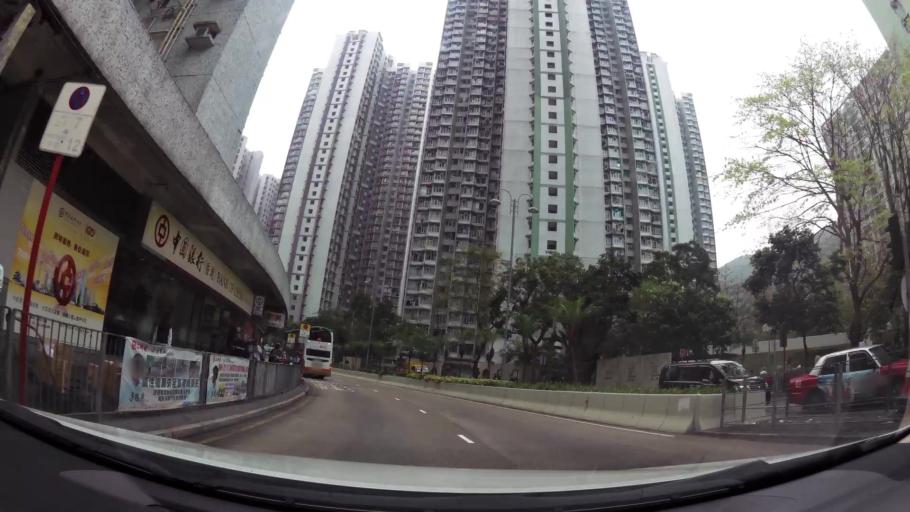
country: HK
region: Wanchai
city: Wan Chai
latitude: 22.2627
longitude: 114.2497
